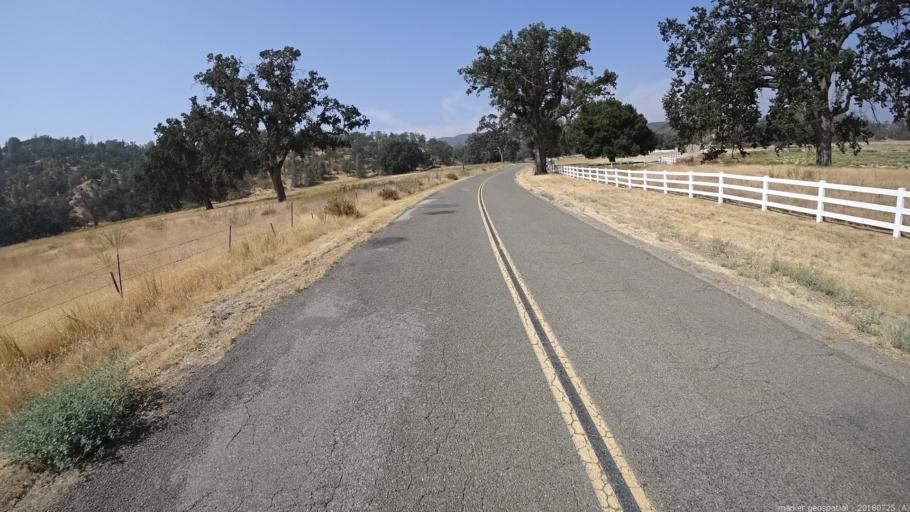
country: US
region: California
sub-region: Fresno County
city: Coalinga
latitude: 35.9258
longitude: -120.5038
